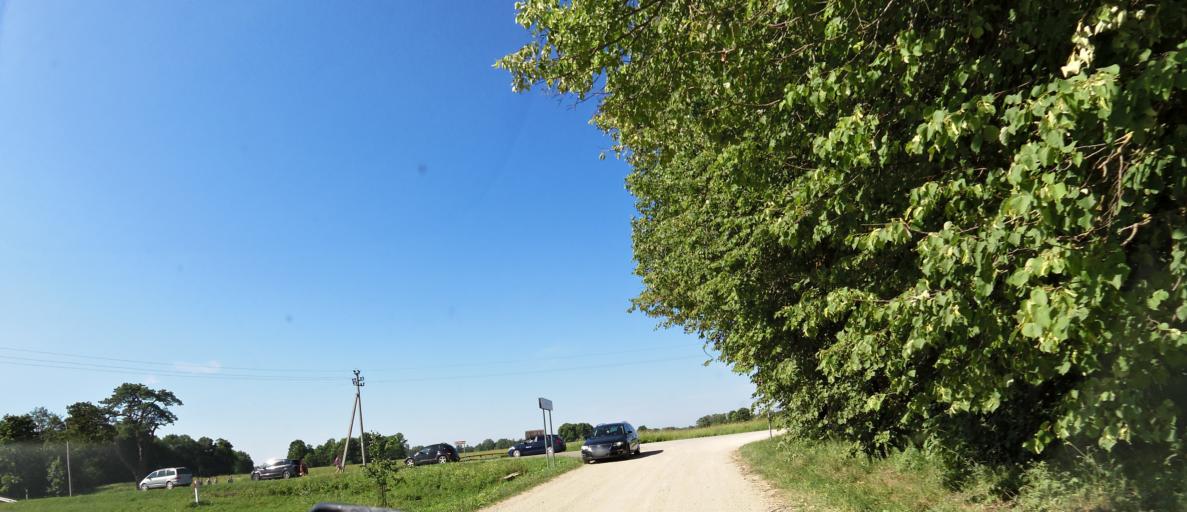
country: LT
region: Panevezys
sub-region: Birzai
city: Birzai
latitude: 56.2095
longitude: 24.6930
